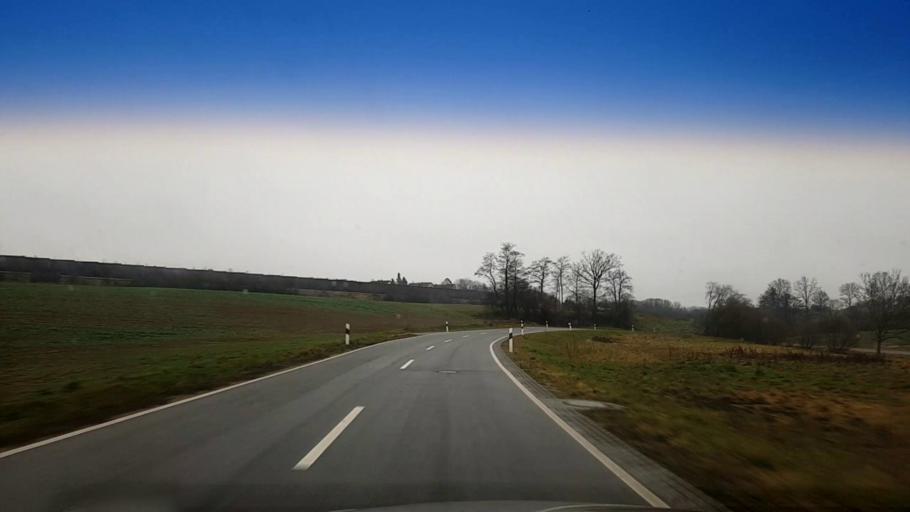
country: DE
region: Bavaria
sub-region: Upper Franconia
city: Memmelsdorf
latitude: 49.9514
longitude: 10.9683
